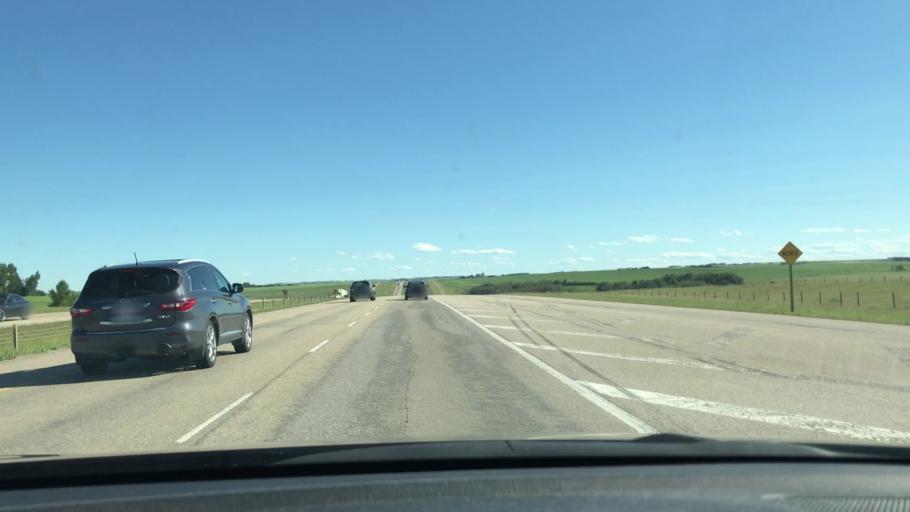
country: CA
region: Alberta
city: Carstairs
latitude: 51.5588
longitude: -114.0253
